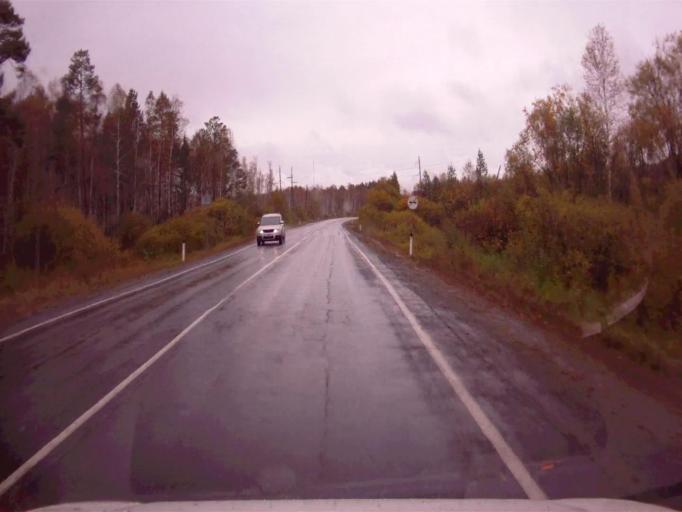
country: RU
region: Chelyabinsk
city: Verkhniy Ufaley
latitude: 55.9911
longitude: 60.3337
